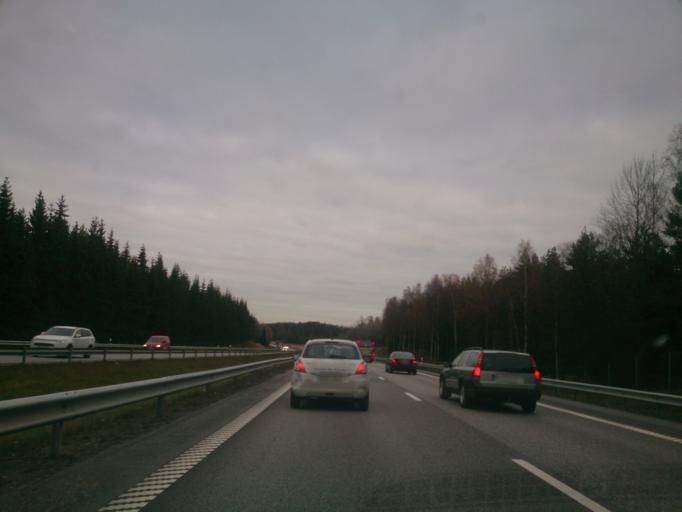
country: SE
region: Stockholm
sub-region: Sodertalje Kommun
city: Pershagen
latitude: 59.1003
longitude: 17.6076
